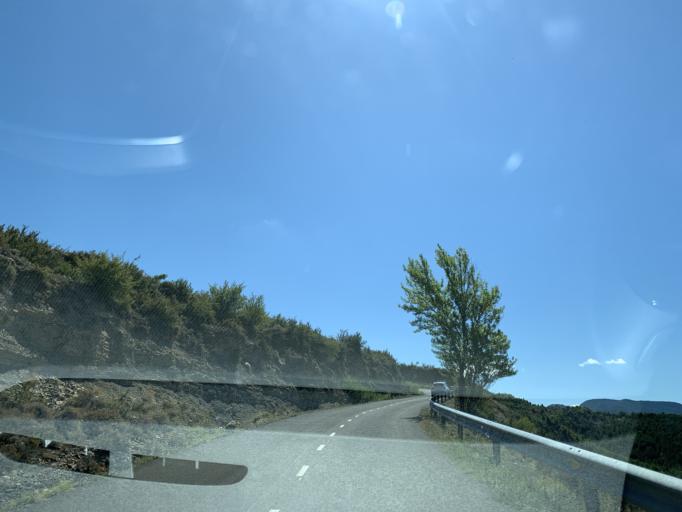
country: ES
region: Aragon
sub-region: Provincia de Huesca
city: Sabinanigo
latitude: 42.5213
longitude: -0.3271
